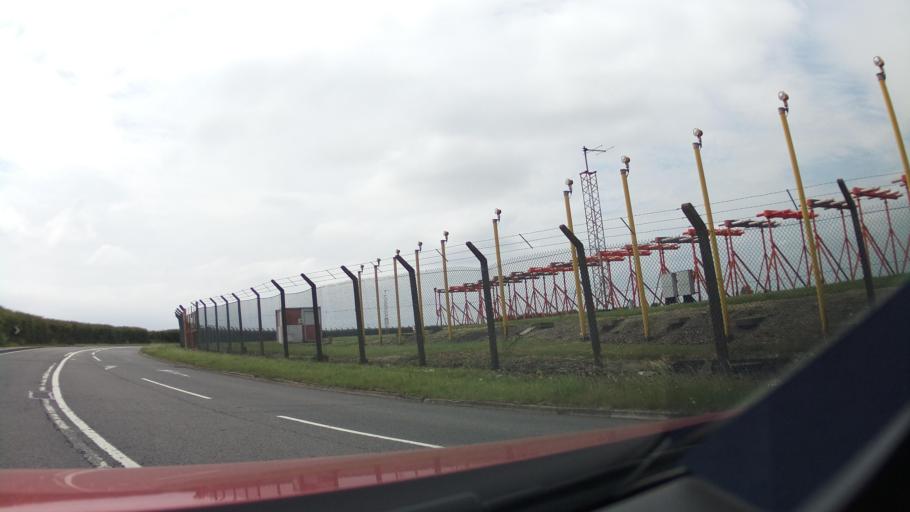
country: GB
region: Wales
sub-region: Vale of Glamorgan
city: Rhoose
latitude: 51.3914
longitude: -3.3259
